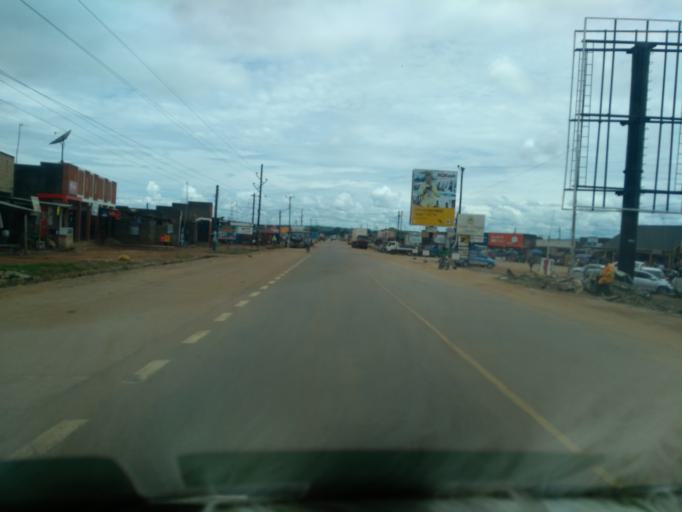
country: UG
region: Central Region
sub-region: Butambala District
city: Gombe
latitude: -0.0120
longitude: 32.0316
